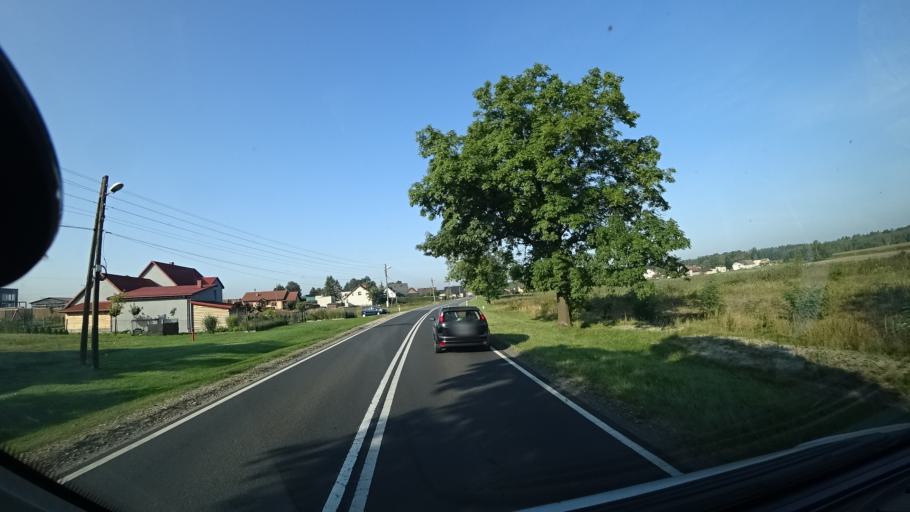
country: PL
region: Silesian Voivodeship
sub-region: Powiat gliwicki
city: Sosnicowice
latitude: 50.2717
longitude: 18.4503
